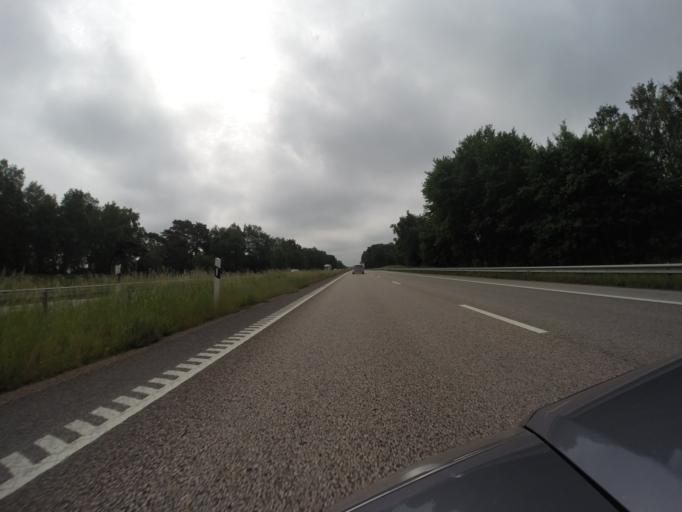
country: SE
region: Skane
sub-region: Kavlinge Kommun
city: Hofterup
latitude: 55.8108
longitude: 12.9471
